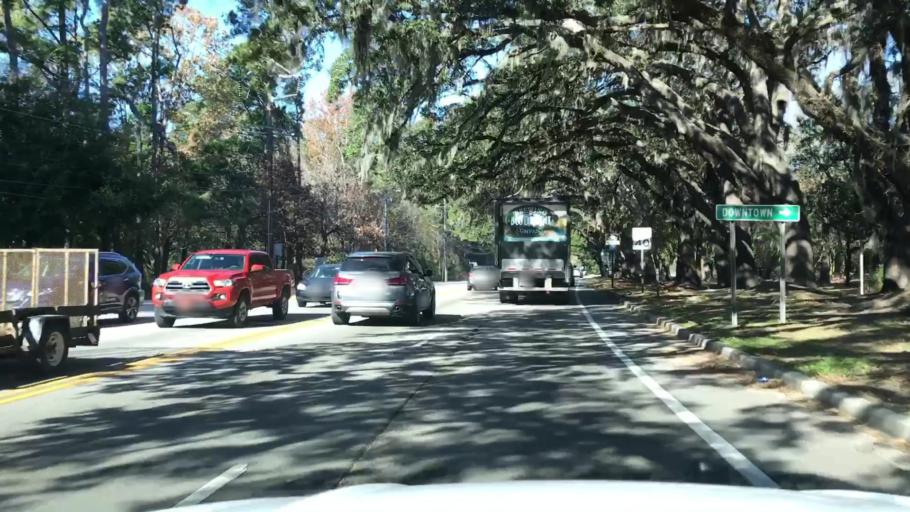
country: US
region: South Carolina
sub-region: Charleston County
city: Charleston
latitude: 32.7467
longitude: -79.9706
